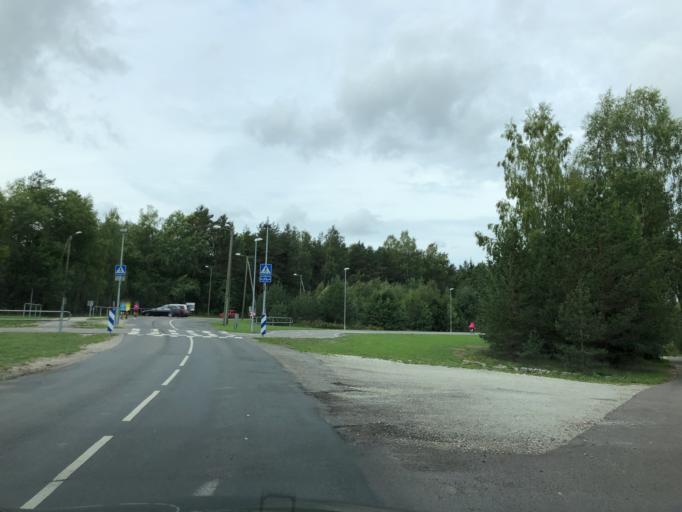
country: EE
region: Harju
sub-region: Saue vald
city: Laagri
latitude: 59.3867
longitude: 24.6291
